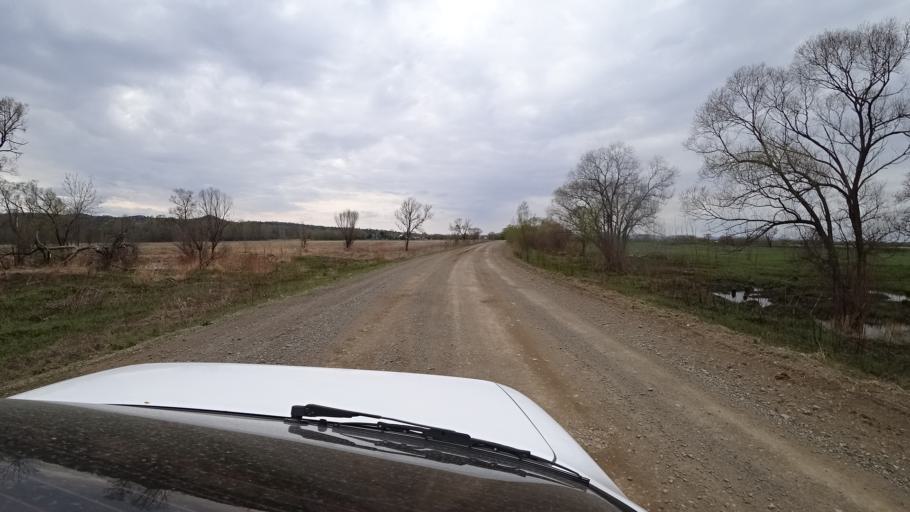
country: RU
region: Primorskiy
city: Novopokrovka
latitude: 45.4901
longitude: 134.4579
